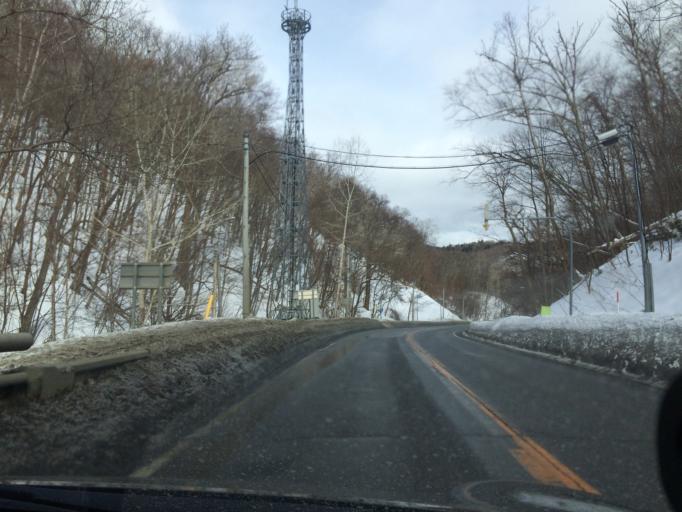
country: JP
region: Hokkaido
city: Shimo-furano
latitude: 42.8881
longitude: 142.2382
